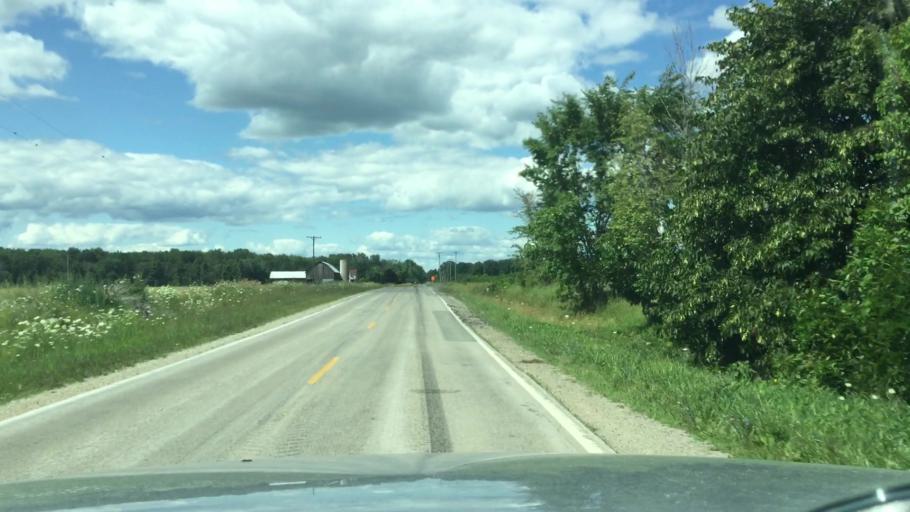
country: US
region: Michigan
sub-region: Saginaw County
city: Hemlock
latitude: 43.3610
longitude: -84.1903
